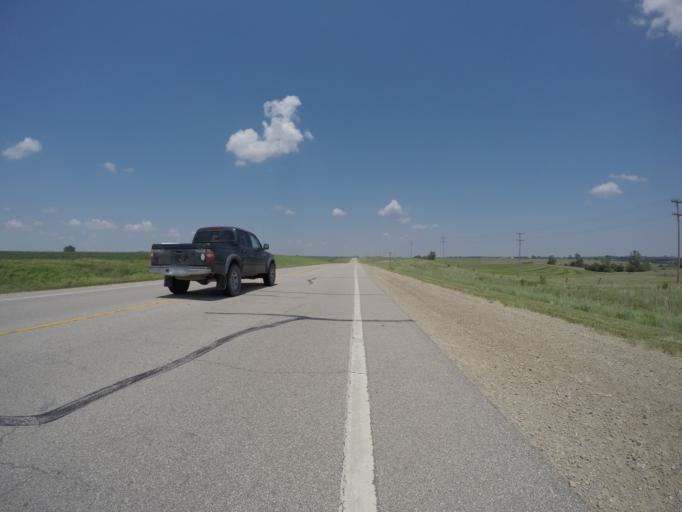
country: US
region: Kansas
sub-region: Doniphan County
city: Troy
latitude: 39.7419
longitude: -95.1438
